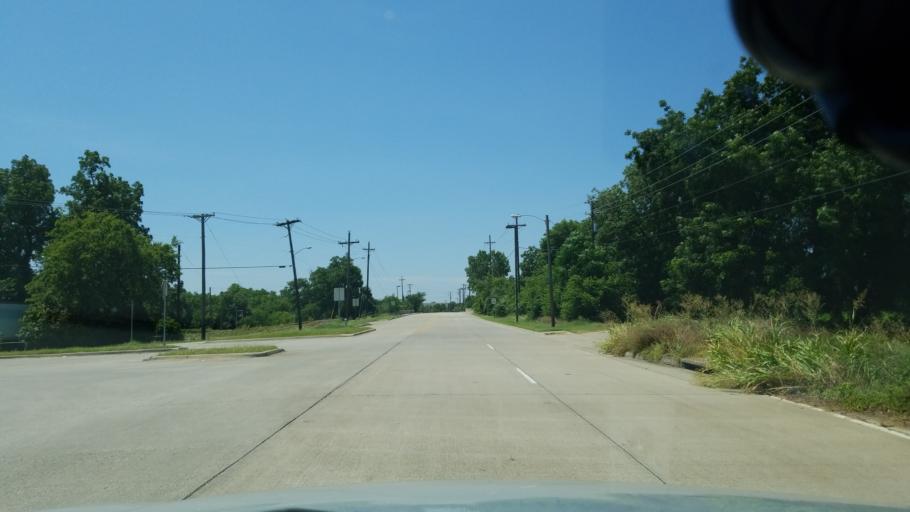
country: US
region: Texas
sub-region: Tarrant County
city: Euless
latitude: 32.8344
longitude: -97.0303
